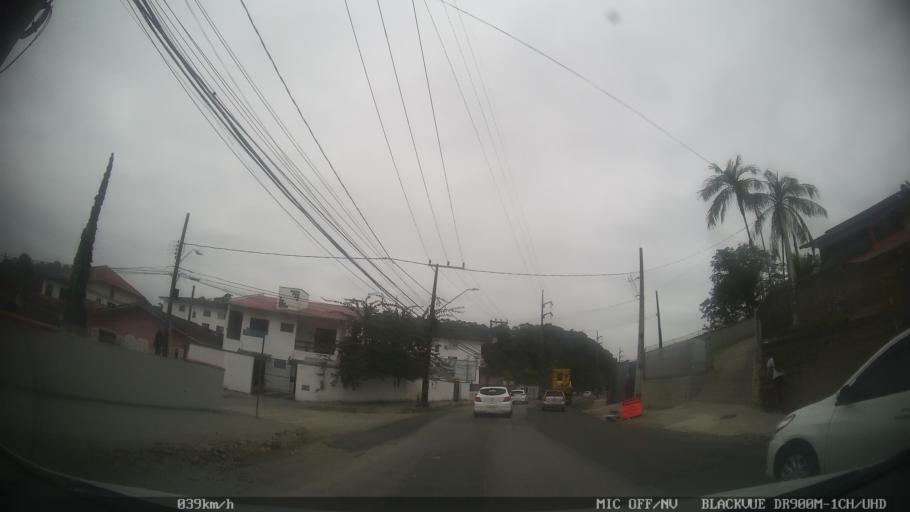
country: BR
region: Santa Catarina
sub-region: Joinville
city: Joinville
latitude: -26.3064
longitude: -48.8301
